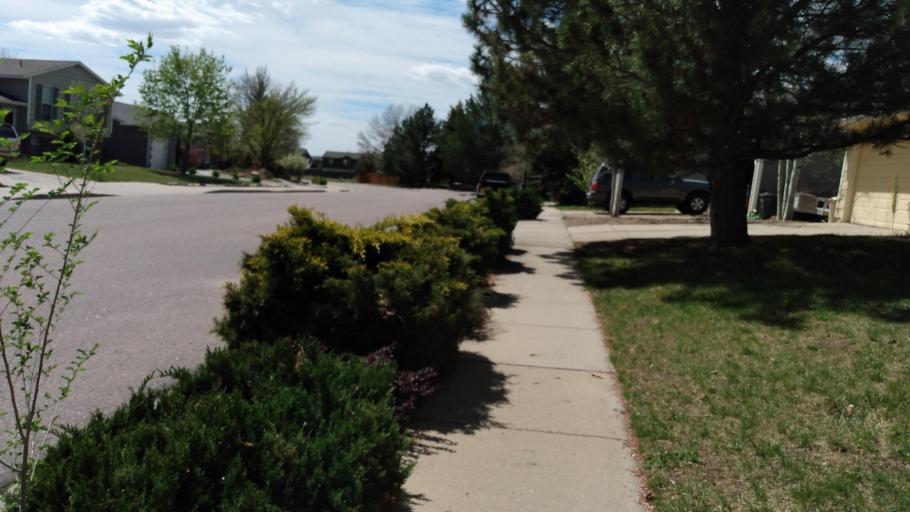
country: US
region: Colorado
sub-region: Boulder County
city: Lafayette
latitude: 40.0090
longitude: -105.0967
